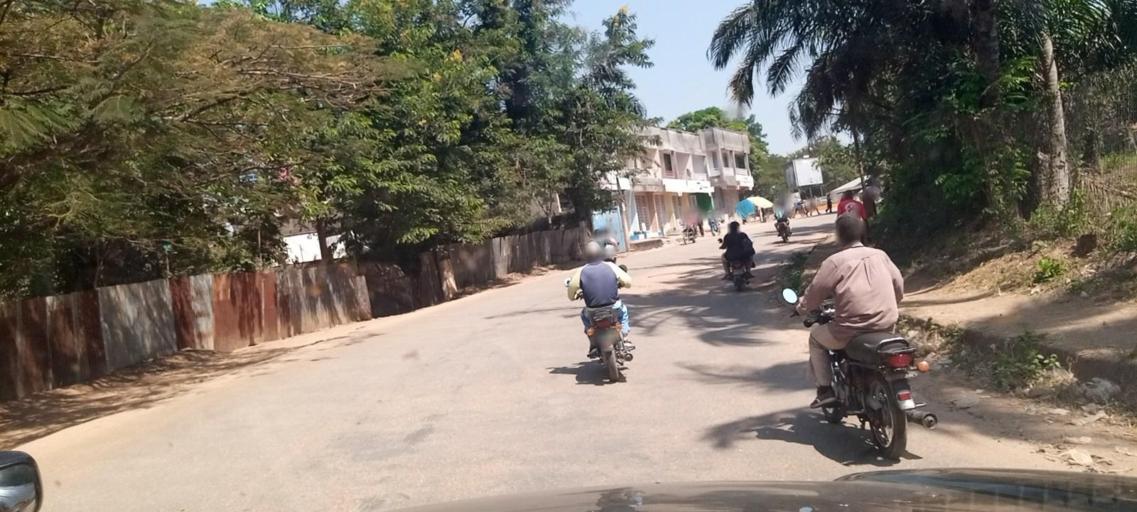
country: CD
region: Kasai-Oriental
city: Mbuji-Mayi
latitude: -6.1234
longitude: 23.5939
